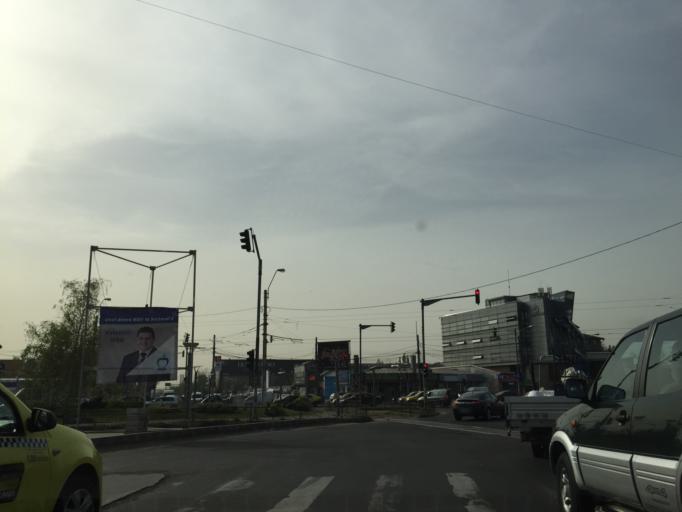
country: RO
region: Bucuresti
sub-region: Municipiul Bucuresti
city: Bucuresti
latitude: 44.4295
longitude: 26.0609
